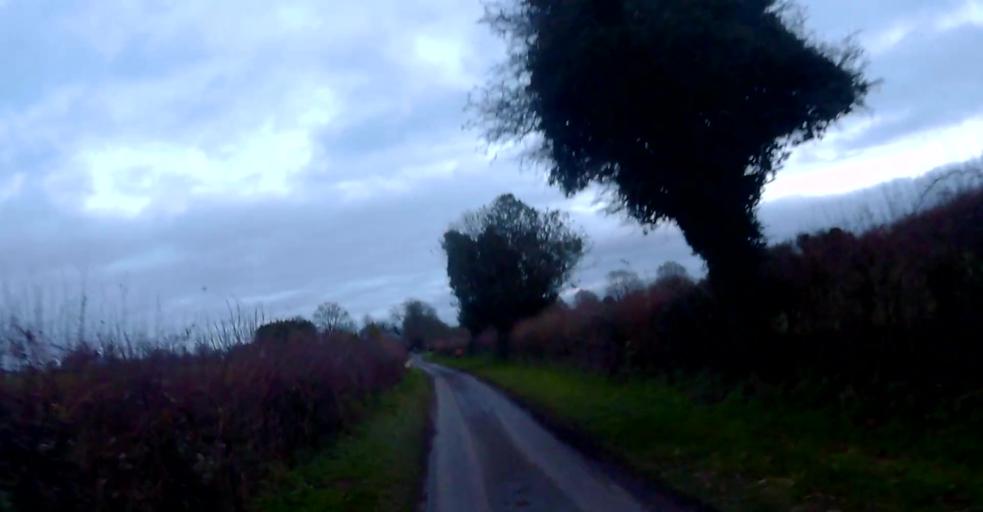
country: GB
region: England
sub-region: Hampshire
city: Overton
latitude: 51.2561
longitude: -1.2093
